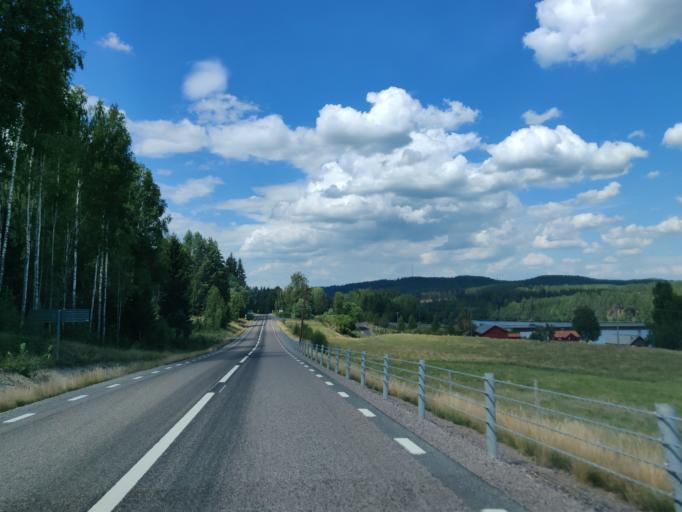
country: SE
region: Vaermland
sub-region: Hagfors Kommun
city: Hagfors
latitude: 59.8771
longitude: 13.7065
